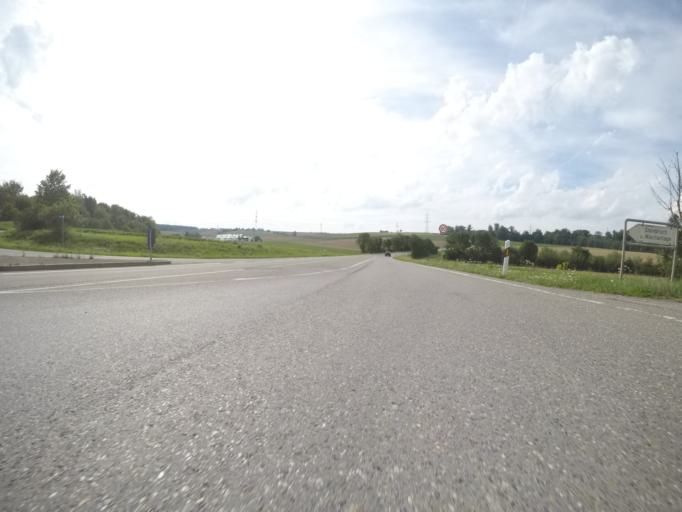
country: DE
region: Baden-Wuerttemberg
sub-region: Regierungsbezirk Stuttgart
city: Hemmingen
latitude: 48.8427
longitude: 9.0069
